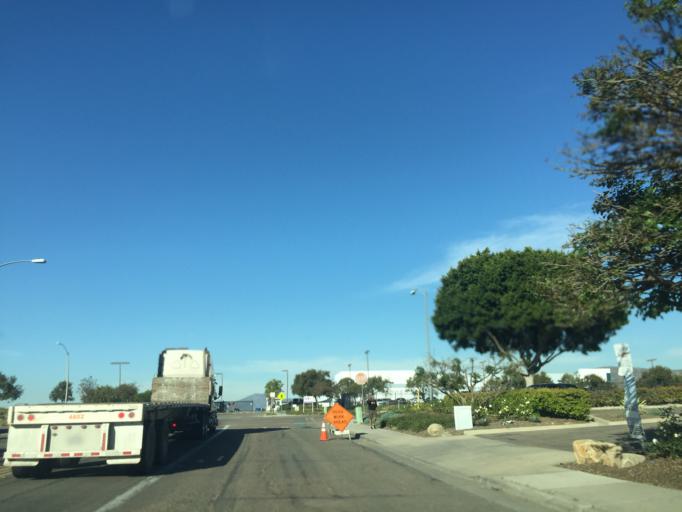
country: MX
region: Baja California
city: Tijuana
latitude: 32.5596
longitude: -116.9359
